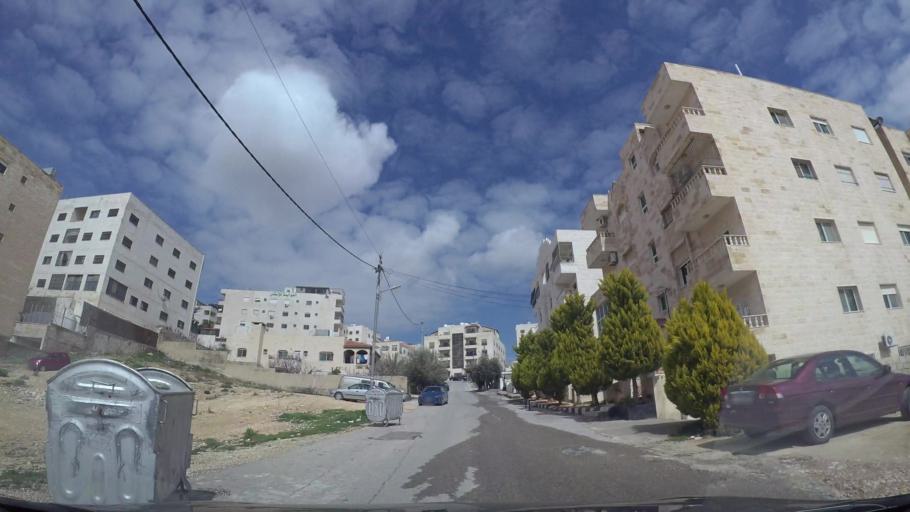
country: JO
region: Amman
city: Amman
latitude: 31.9969
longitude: 35.9160
